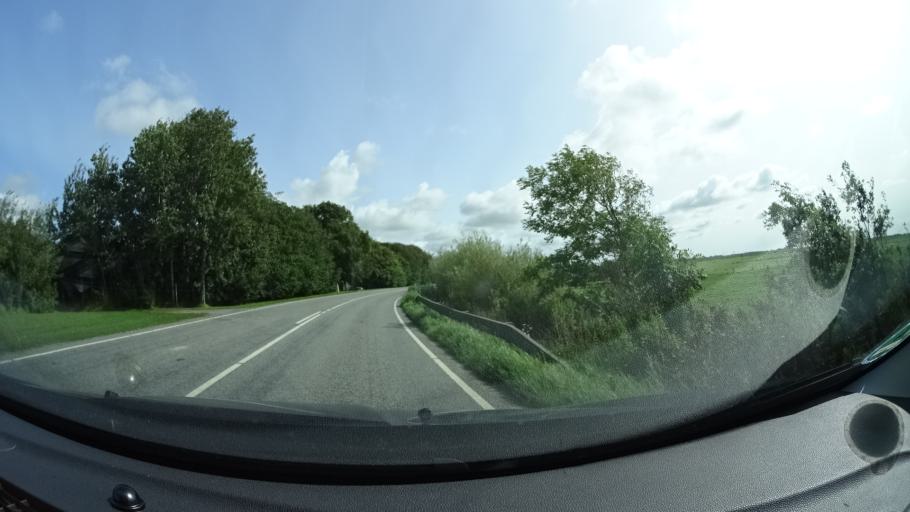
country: DE
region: Schleswig-Holstein
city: Neukirchen
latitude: 54.9141
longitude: 8.7402
